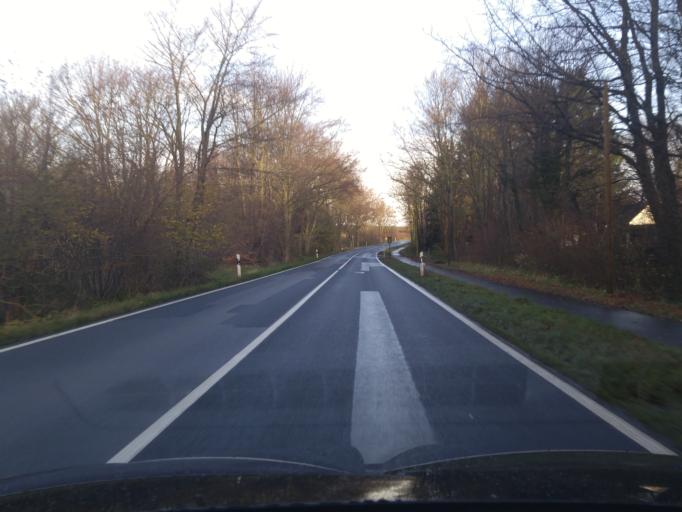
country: DE
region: Schleswig-Holstein
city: Ratekau
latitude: 53.9617
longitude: 10.7594
